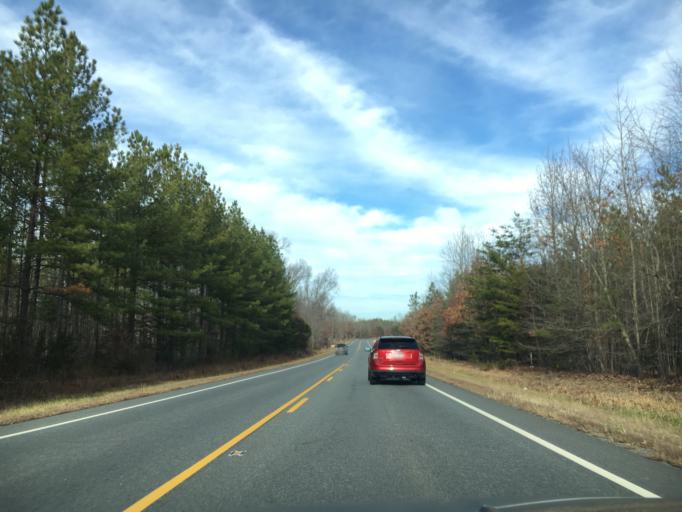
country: US
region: Virginia
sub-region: Louisa County
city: Louisa
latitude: 38.0540
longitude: -77.8806
